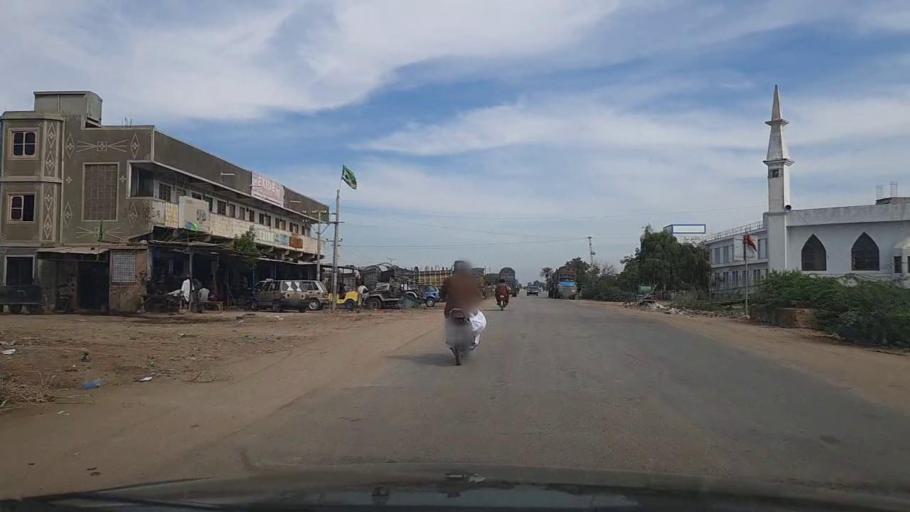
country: PK
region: Sindh
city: Thatta
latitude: 24.7552
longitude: 67.9282
